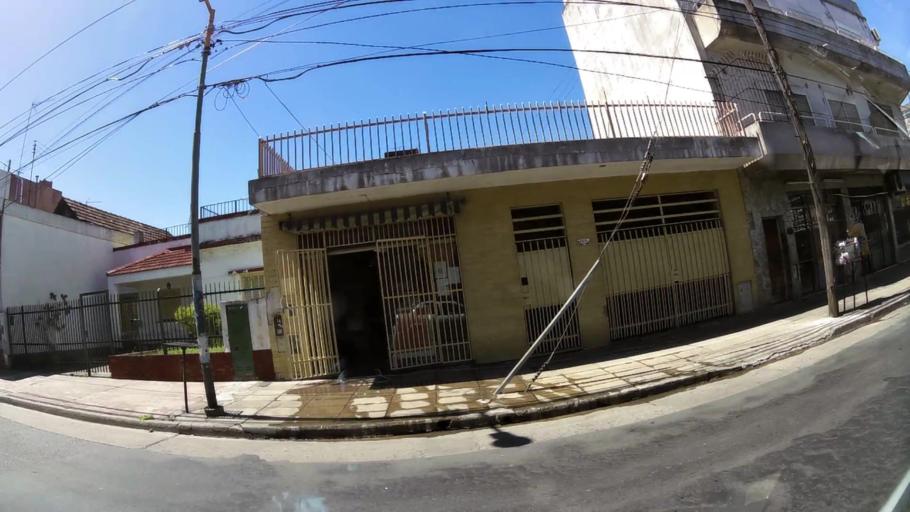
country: AR
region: Buenos Aires
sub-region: Partido de General San Martin
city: General San Martin
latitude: -34.5884
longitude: -58.5277
